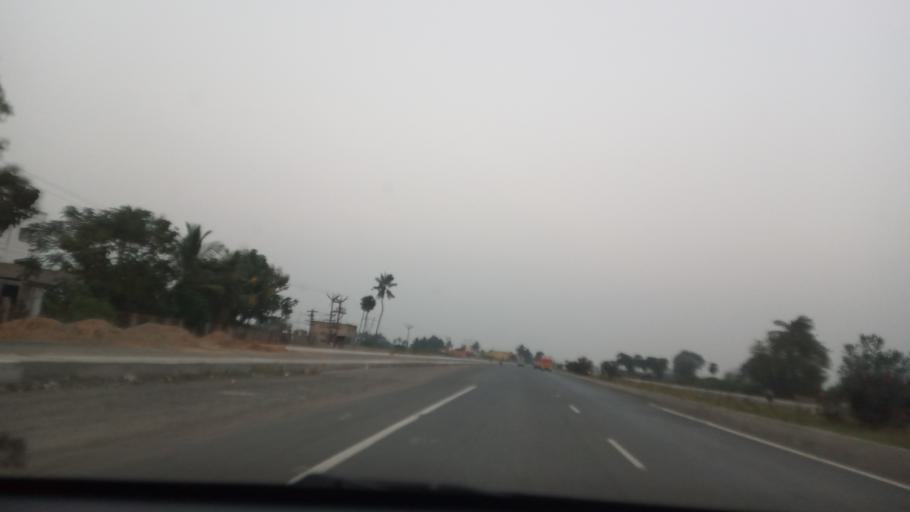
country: IN
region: Tamil Nadu
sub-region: Kancheepuram
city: Kanchipuram
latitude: 12.8735
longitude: 79.6706
